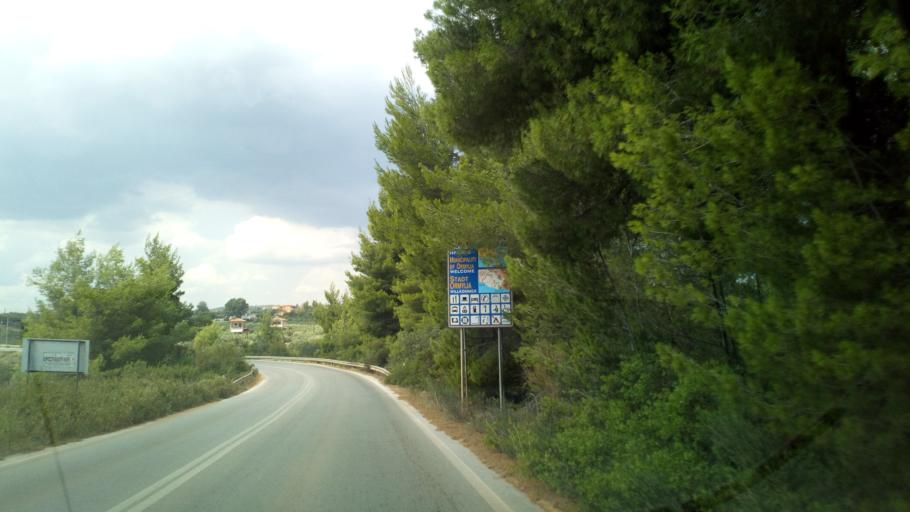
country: GR
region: Central Macedonia
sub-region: Nomos Chalkidikis
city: Nikiti
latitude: 40.2307
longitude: 23.6073
